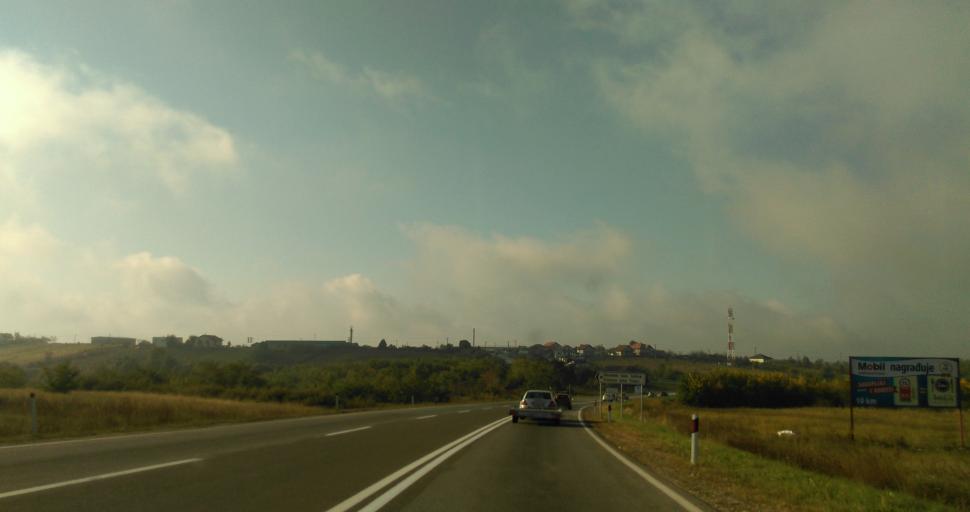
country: RS
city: Rusanj
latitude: 44.6542
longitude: 20.4316
